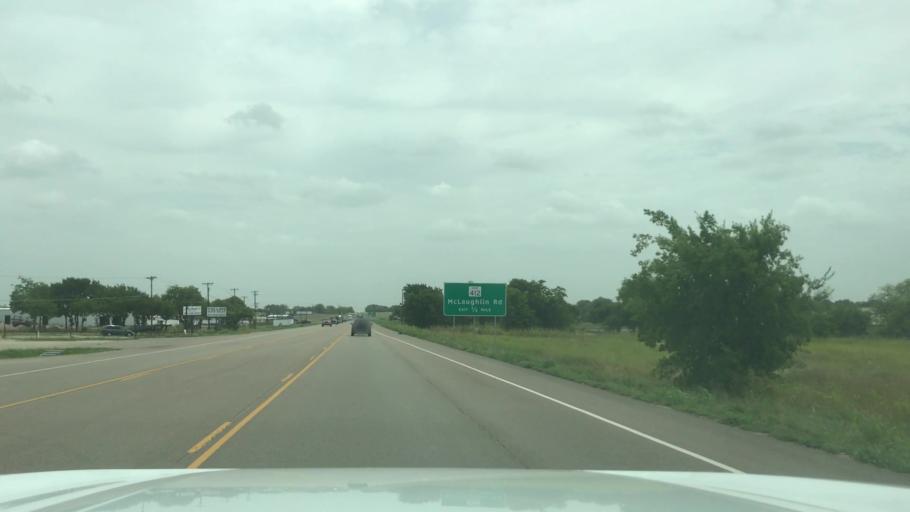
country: US
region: Texas
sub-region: McLennan County
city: Woodway
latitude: 31.5792
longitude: -97.2998
